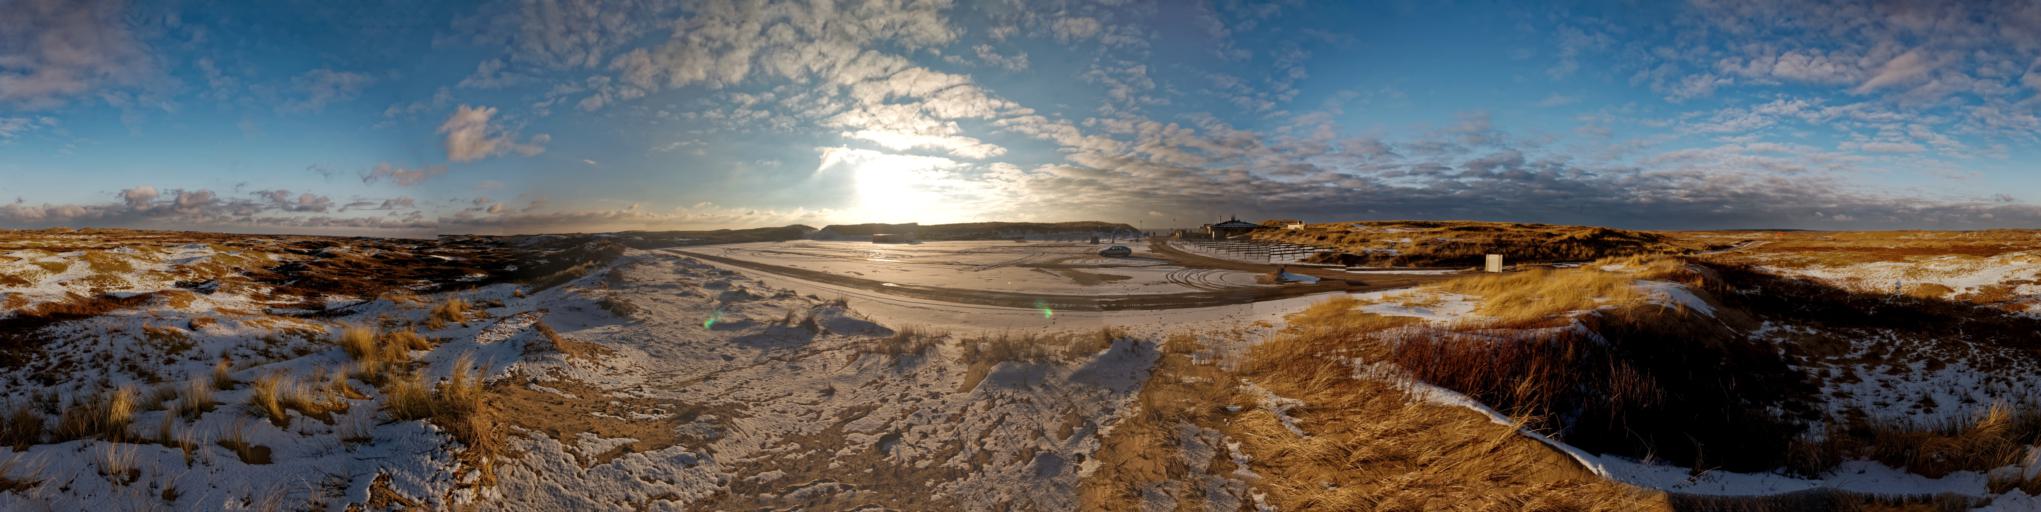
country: NL
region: North Holland
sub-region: Gemeente Den Helder
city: Den Helder
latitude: 53.0209
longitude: 4.7125
